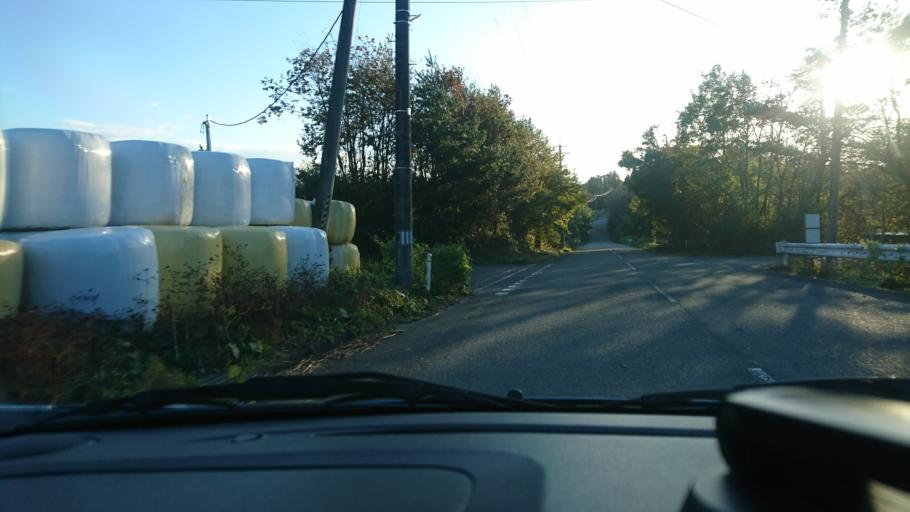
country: JP
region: Iwate
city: Ichinoseki
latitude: 38.7909
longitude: 141.2349
